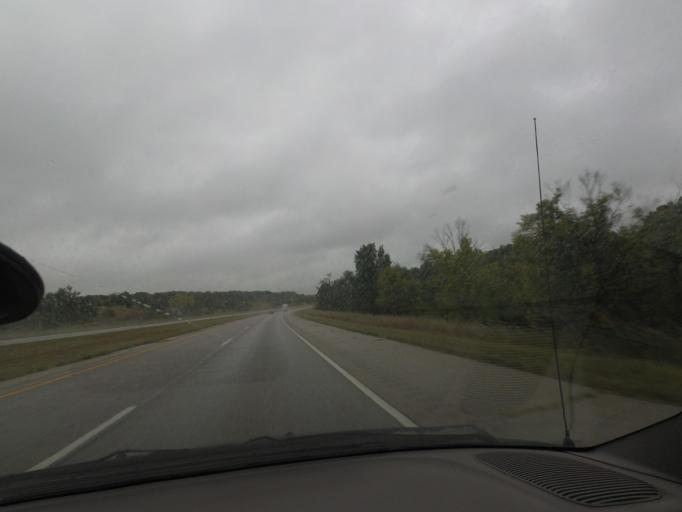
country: US
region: Illinois
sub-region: Pike County
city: Barry
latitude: 39.7243
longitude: -91.1157
